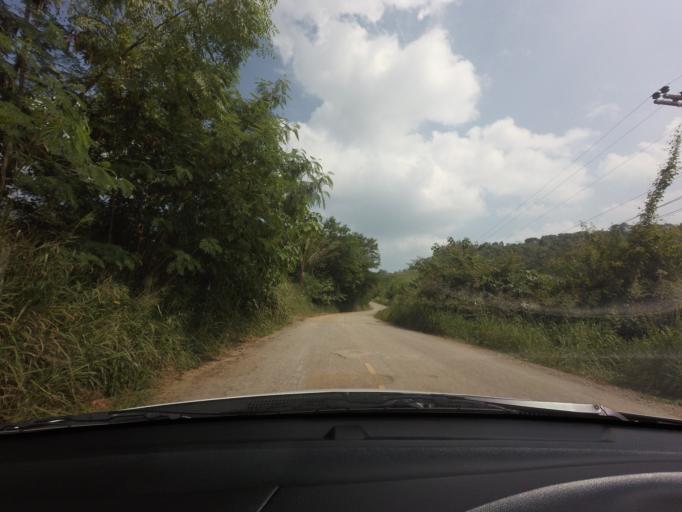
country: TH
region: Nakhon Ratchasima
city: Pak Chong
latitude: 14.5447
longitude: 101.5907
